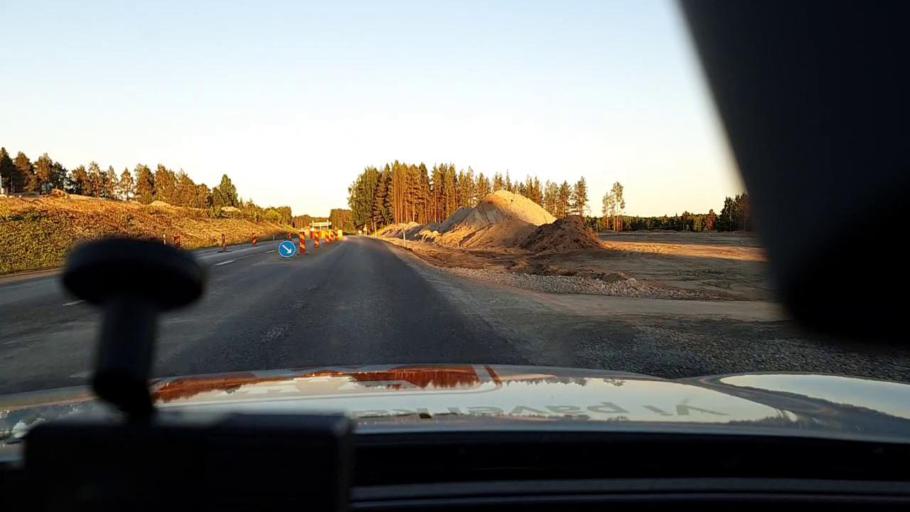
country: SE
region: Norrbotten
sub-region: Bodens Kommun
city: Saevast
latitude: 65.7216
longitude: 21.7908
